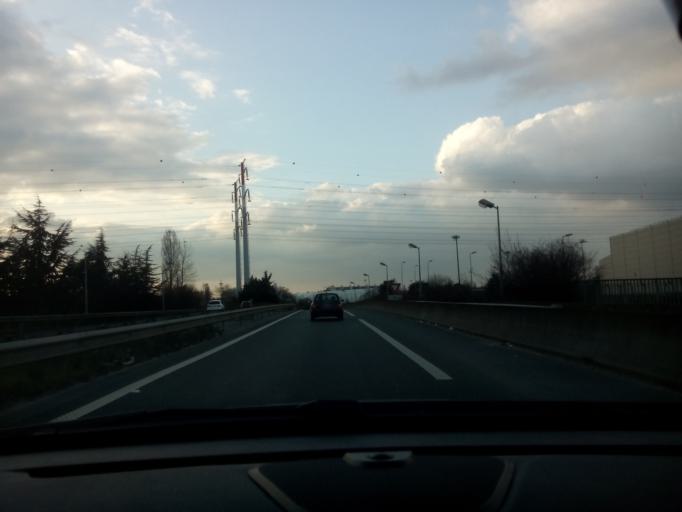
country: FR
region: Ile-de-France
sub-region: Departement du Val-de-Marne
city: Chevilly-Larue
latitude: 48.7579
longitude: 2.3399
